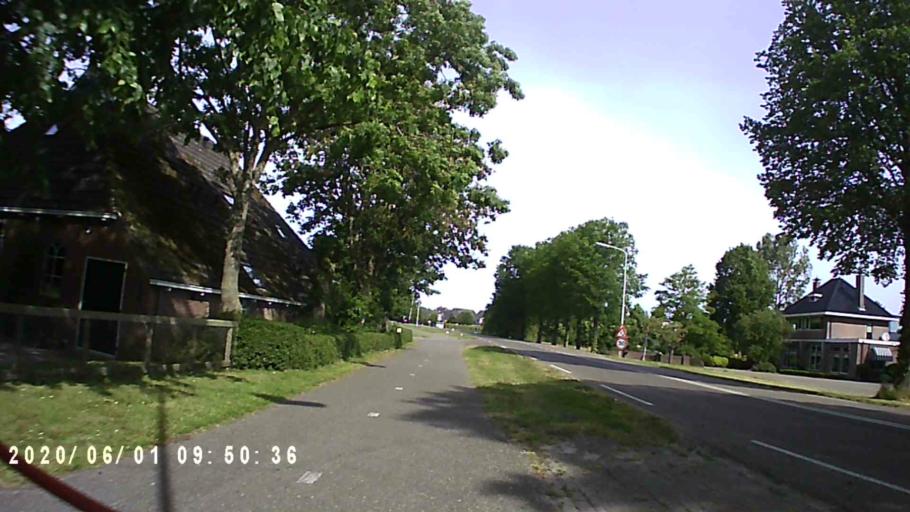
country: NL
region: Friesland
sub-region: Menameradiel
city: Berltsum
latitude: 53.2422
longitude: 5.6616
